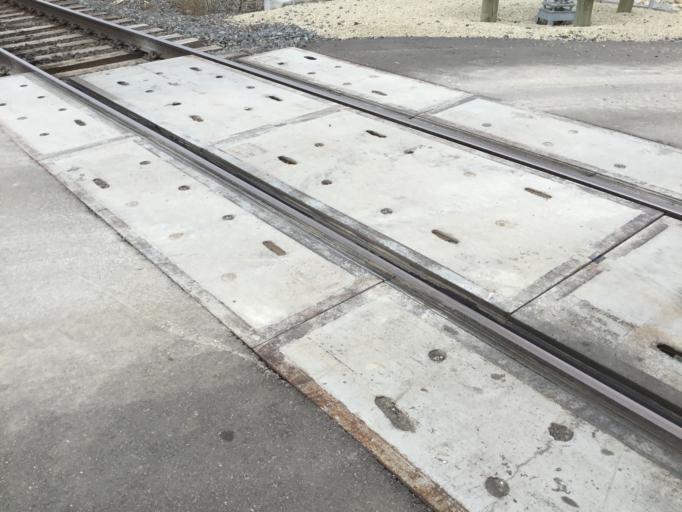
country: US
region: Kansas
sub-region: Dickinson County
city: Herington
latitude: 38.7413
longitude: -96.8345
